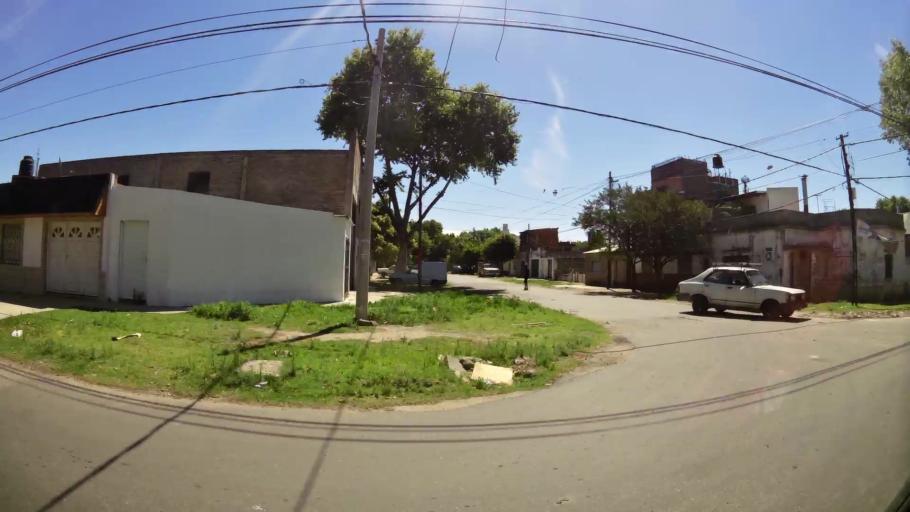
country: AR
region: Santa Fe
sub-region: Departamento de Rosario
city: Rosario
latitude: -32.9340
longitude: -60.6938
